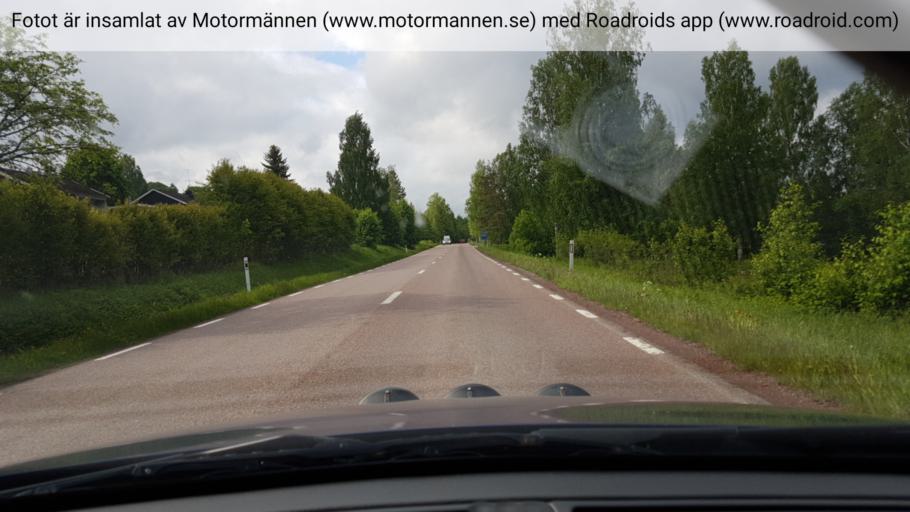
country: SE
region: Dalarna
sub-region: Orsa Kommun
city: Orsa
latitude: 61.0985
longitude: 14.6354
